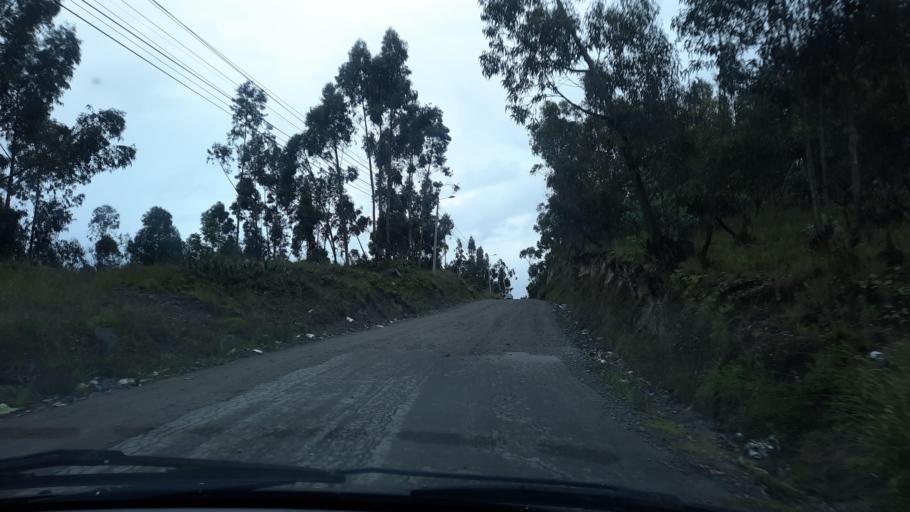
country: EC
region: Chimborazo
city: Riobamba
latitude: -1.6842
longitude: -78.6603
